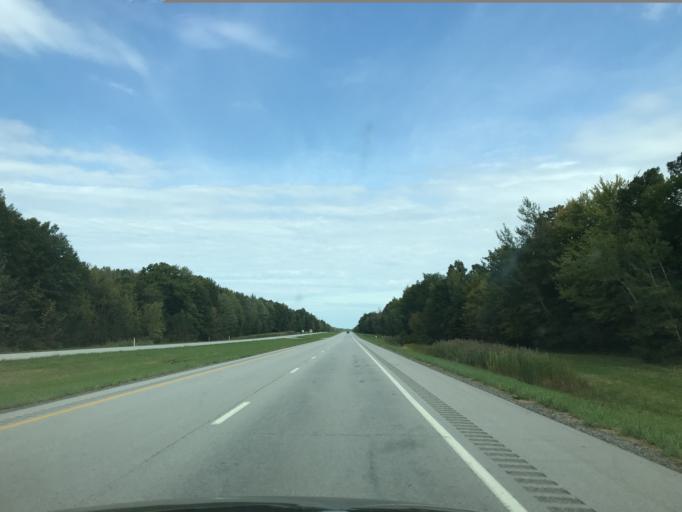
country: US
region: Ohio
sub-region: Ashtabula County
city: Jefferson
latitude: 41.6530
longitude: -80.7133
